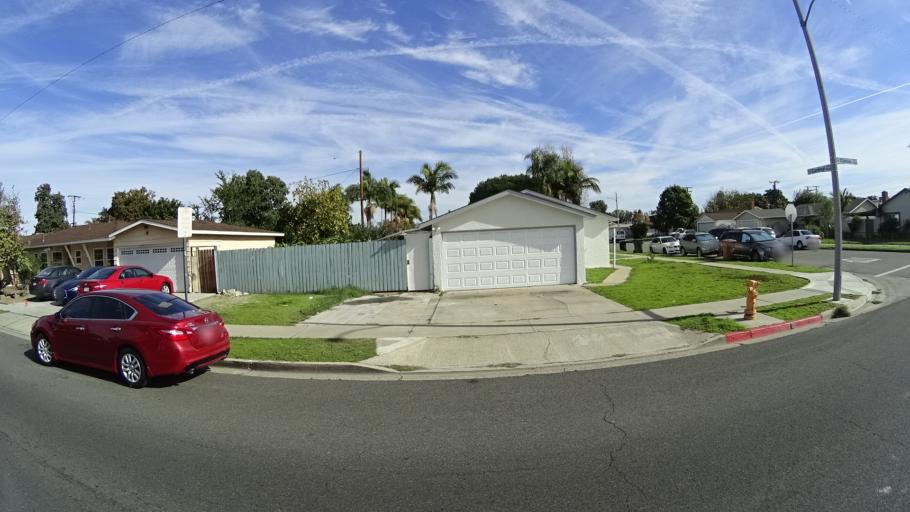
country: US
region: California
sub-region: Orange County
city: Garden Grove
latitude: 33.7659
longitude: -117.9116
